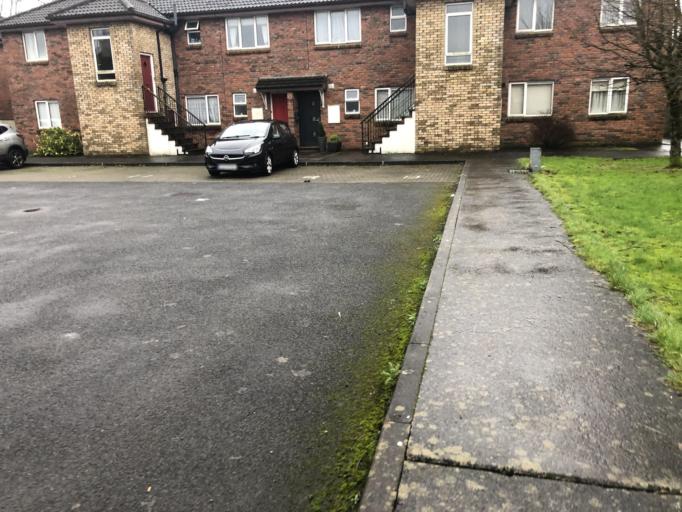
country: IE
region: Connaught
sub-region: County Galway
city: Tuam
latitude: 53.5172
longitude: -8.8446
